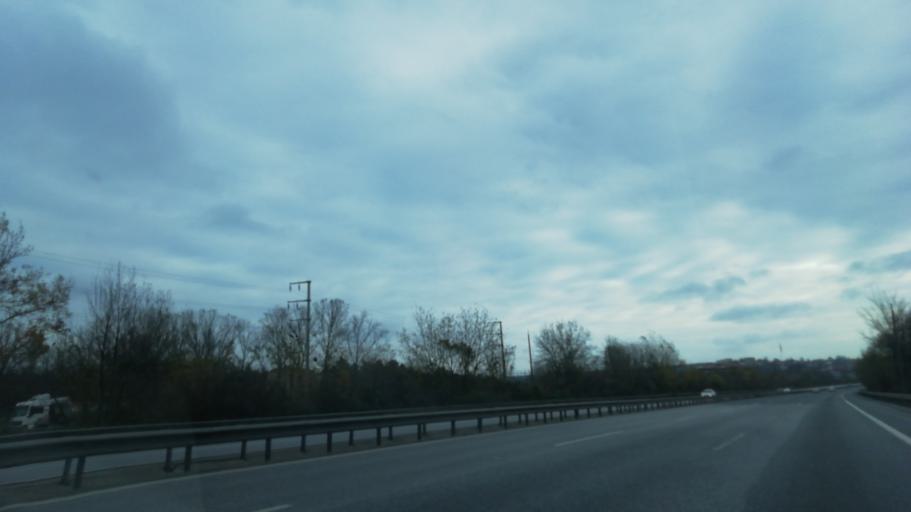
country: TR
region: Kocaeli
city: Derbent
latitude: 40.7240
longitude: 30.0982
